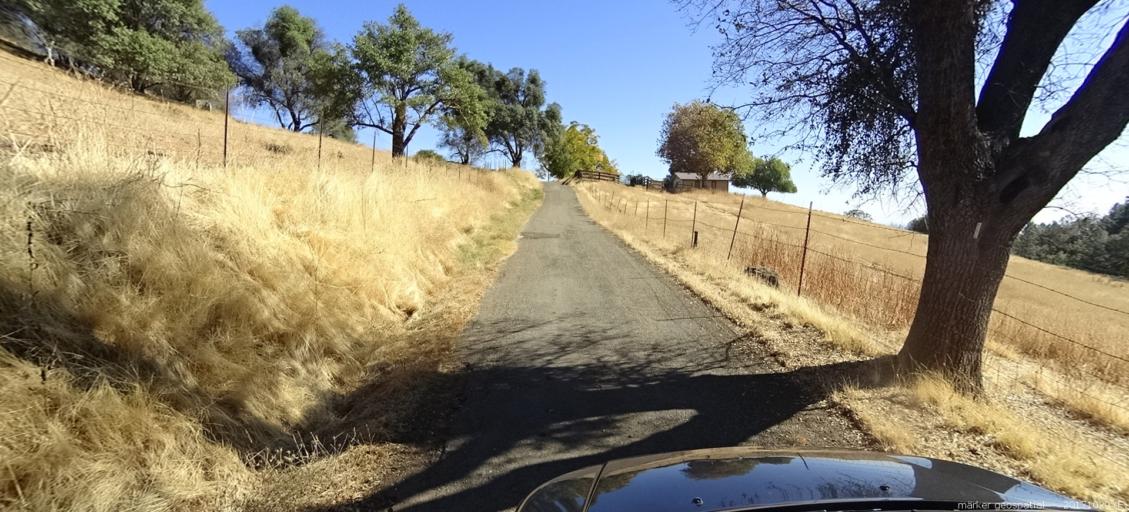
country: US
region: California
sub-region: Shasta County
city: Shasta
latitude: 40.4662
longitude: -122.6904
